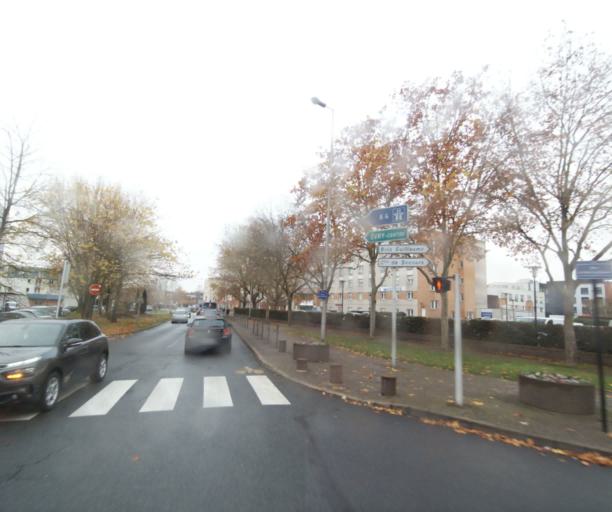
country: FR
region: Ile-de-France
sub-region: Departement de l'Essonne
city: Ris-Orangis
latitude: 48.6387
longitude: 2.4266
